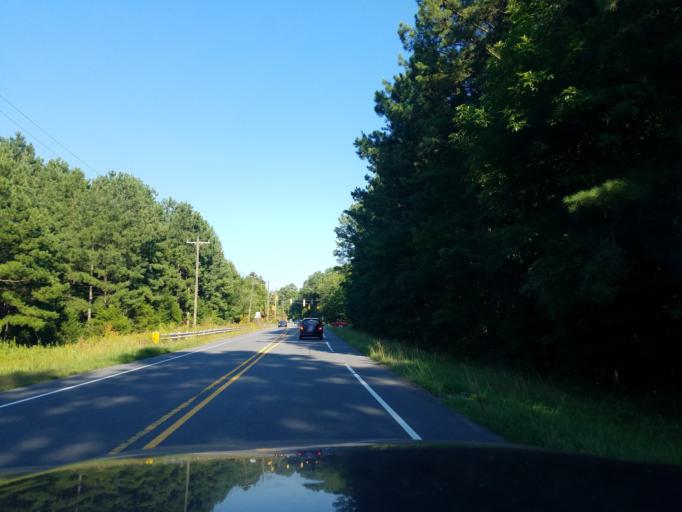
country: US
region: North Carolina
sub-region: Orange County
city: Chapel Hill
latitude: 35.8878
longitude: -78.9897
